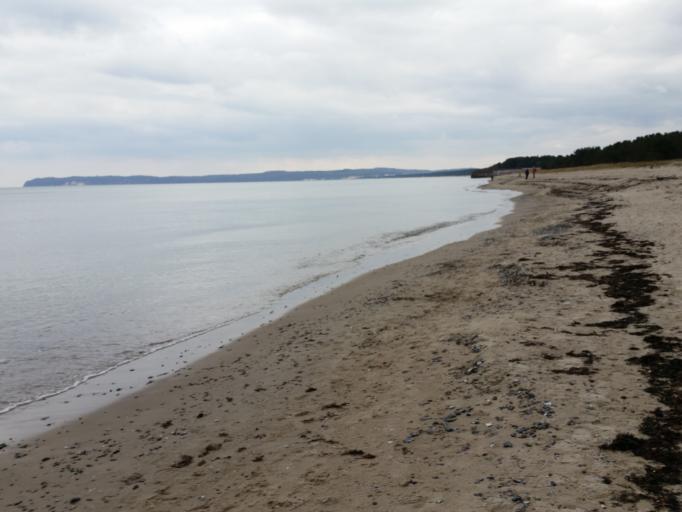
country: DE
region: Mecklenburg-Vorpommern
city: Ostseebad Binz
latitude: 54.4489
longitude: 13.5733
